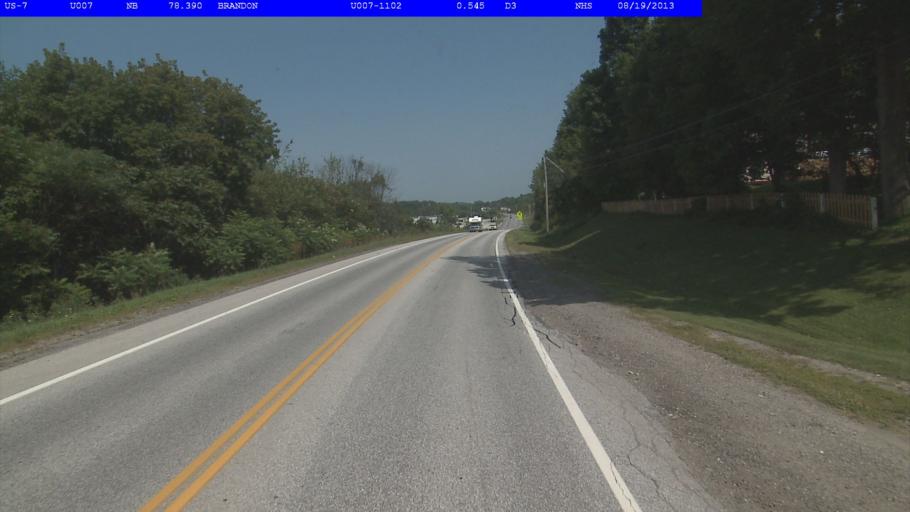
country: US
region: Vermont
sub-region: Rutland County
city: Brandon
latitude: 43.7622
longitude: -73.0498
